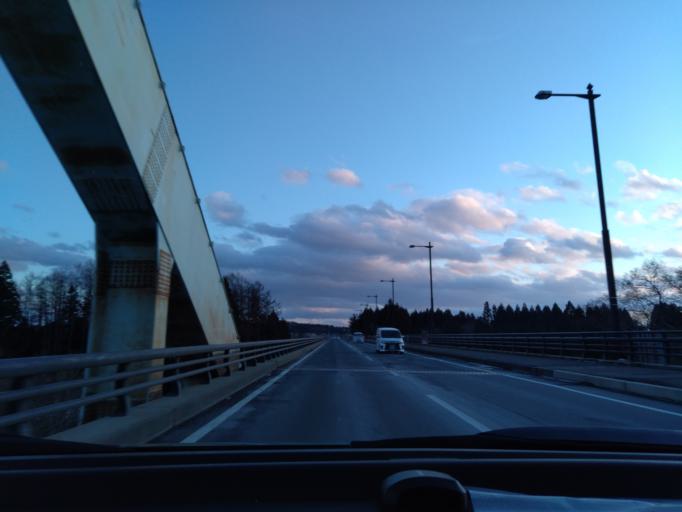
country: JP
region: Iwate
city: Hanamaki
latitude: 39.4004
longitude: 141.1407
